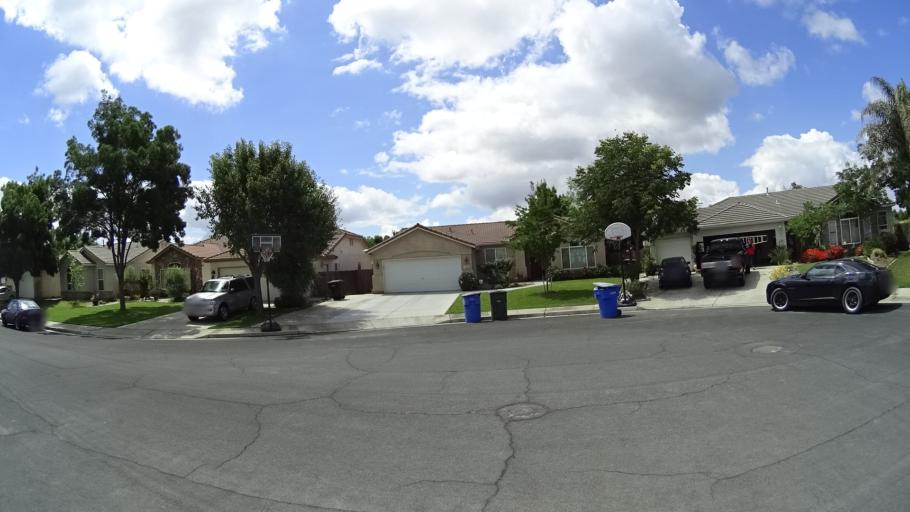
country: US
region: California
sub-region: Kings County
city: Lucerne
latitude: 36.3626
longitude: -119.6633
